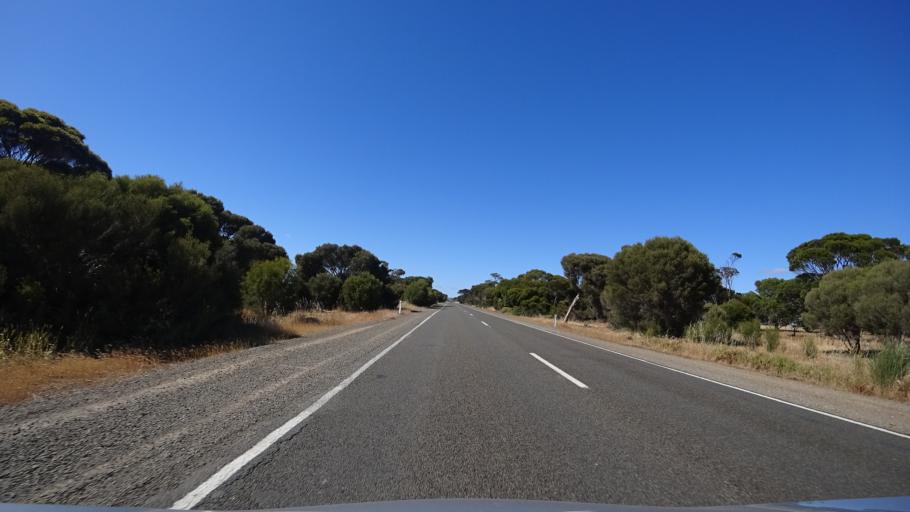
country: AU
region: South Australia
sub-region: Kangaroo Island
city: Kingscote
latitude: -35.6896
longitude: 137.5719
